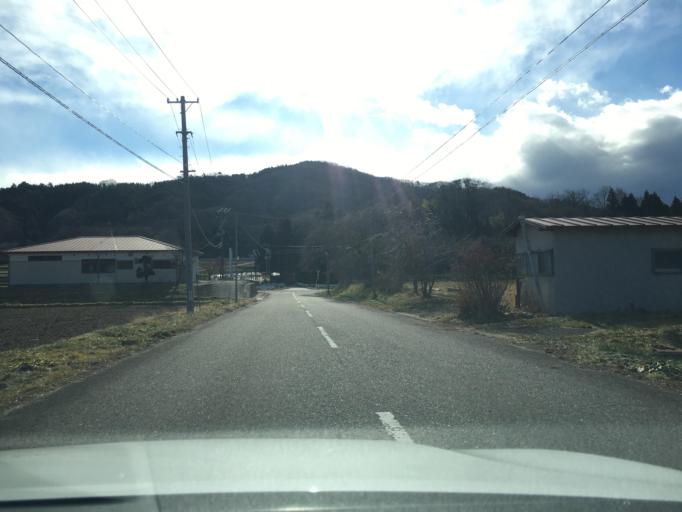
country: JP
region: Fukushima
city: Funehikimachi-funehiki
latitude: 37.3597
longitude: 140.6174
